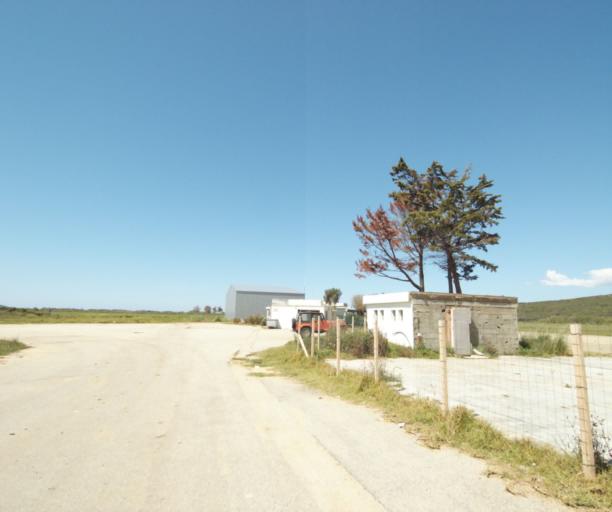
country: FR
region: Corsica
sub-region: Departement de la Corse-du-Sud
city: Propriano
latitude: 41.6589
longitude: 8.8939
